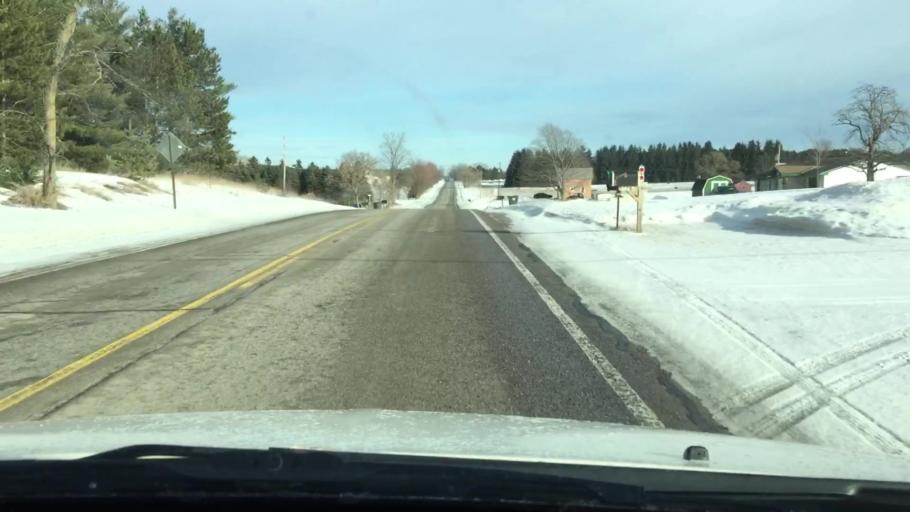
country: US
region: Michigan
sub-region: Kalkaska County
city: Kalkaska
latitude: 44.6403
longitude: -85.2069
